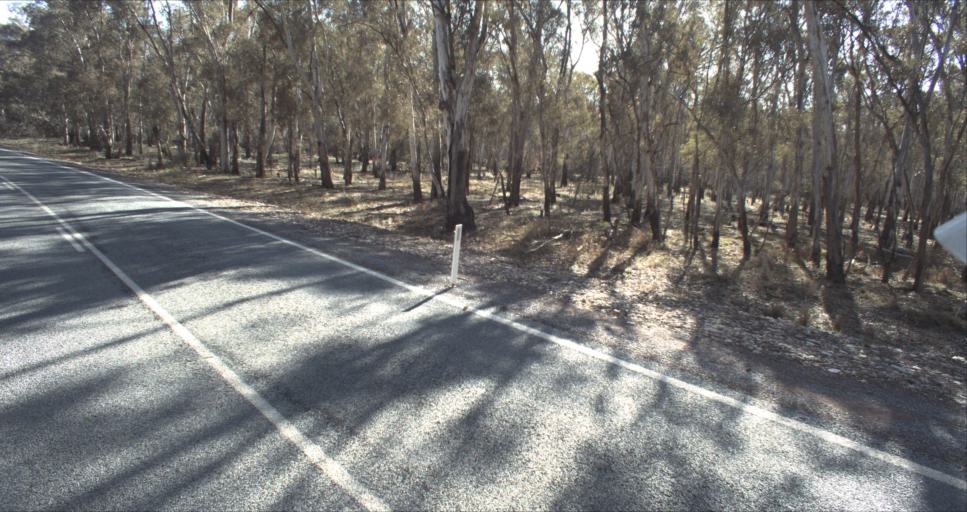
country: AU
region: New South Wales
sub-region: Leeton
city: Leeton
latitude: -34.6251
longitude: 146.3801
